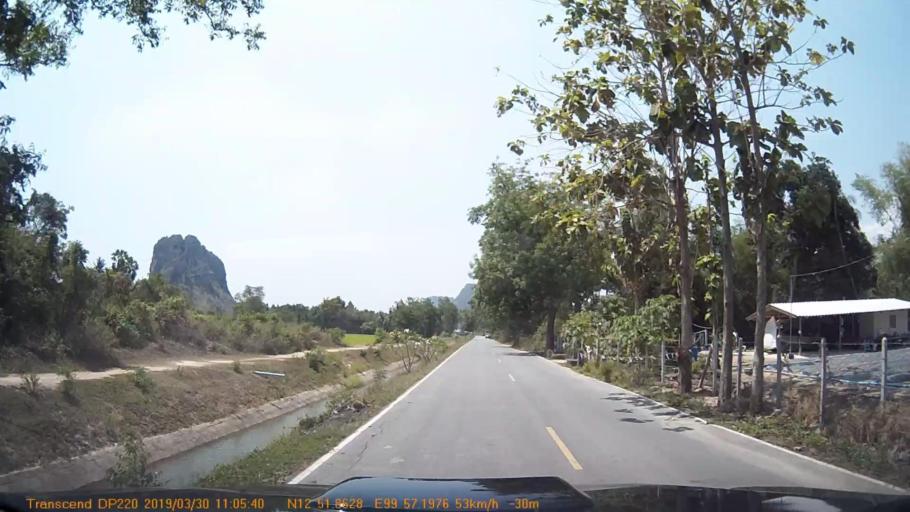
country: TH
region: Phetchaburi
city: Cha-am
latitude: 12.8642
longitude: 99.9533
